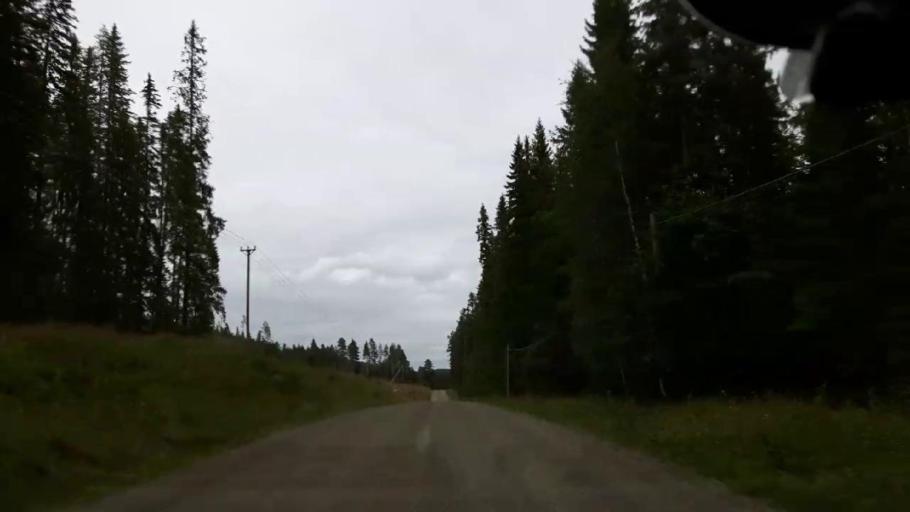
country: SE
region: Jaemtland
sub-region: Braecke Kommun
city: Braecke
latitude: 63.0437
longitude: 15.3550
